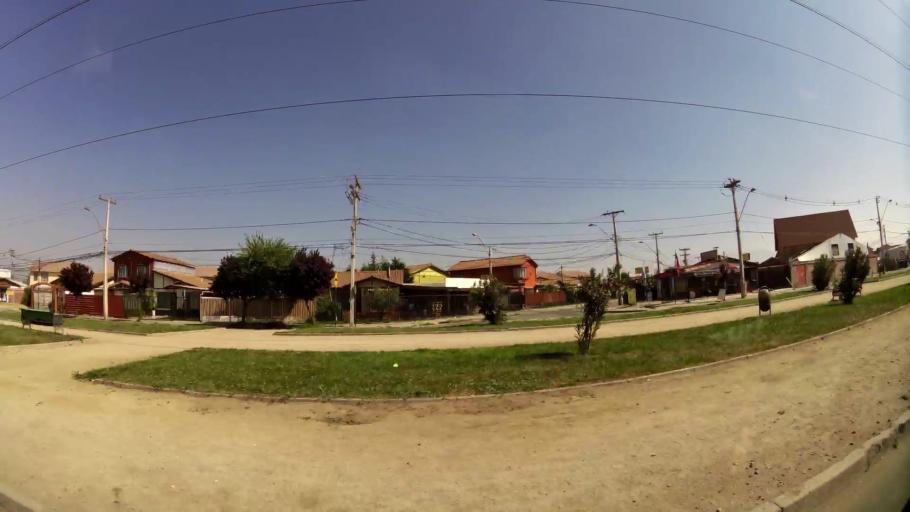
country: CL
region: Santiago Metropolitan
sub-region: Provincia de Santiago
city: Lo Prado
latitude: -33.3496
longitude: -70.7419
